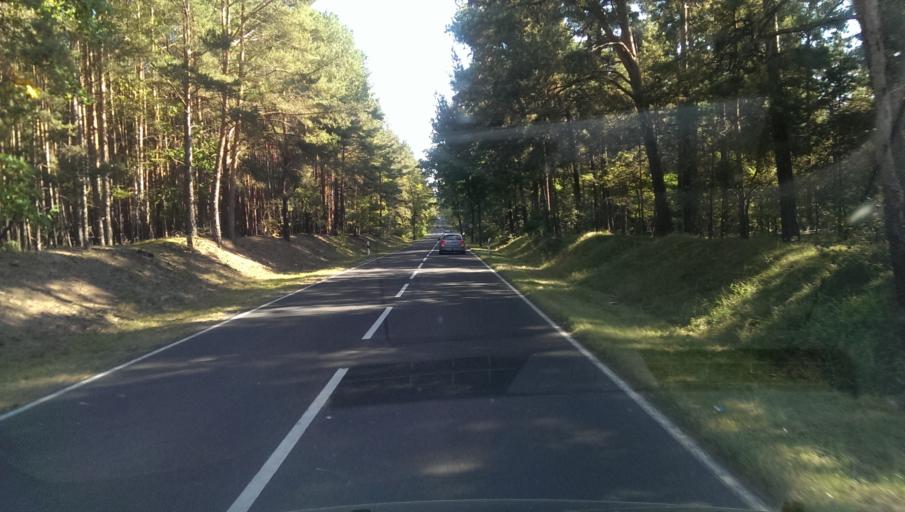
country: DE
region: Brandenburg
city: Teupitz
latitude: 52.1266
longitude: 13.6309
